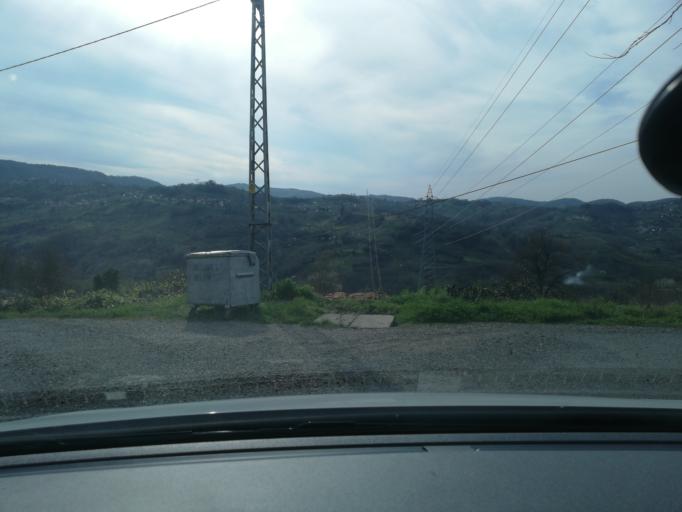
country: TR
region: Zonguldak
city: Kozlu
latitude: 41.3576
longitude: 31.6265
